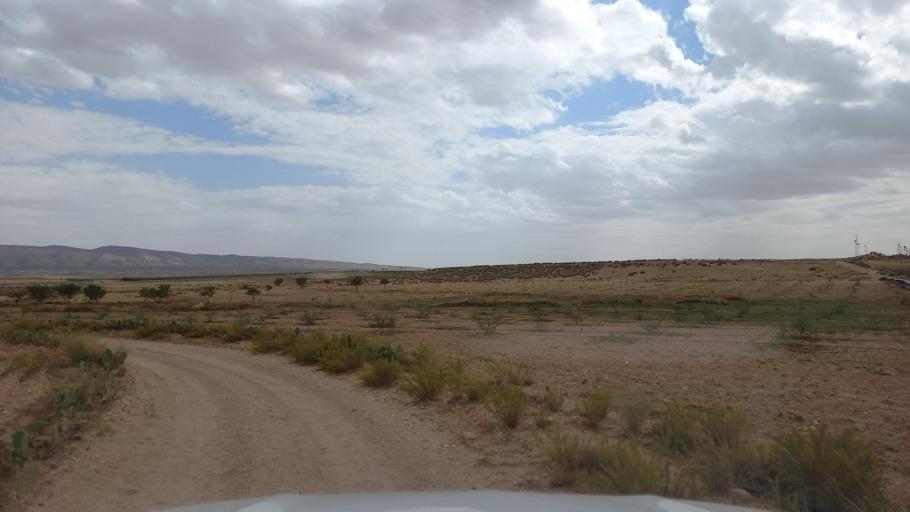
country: TN
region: Al Qasrayn
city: Sbiba
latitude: 35.3840
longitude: 9.1044
